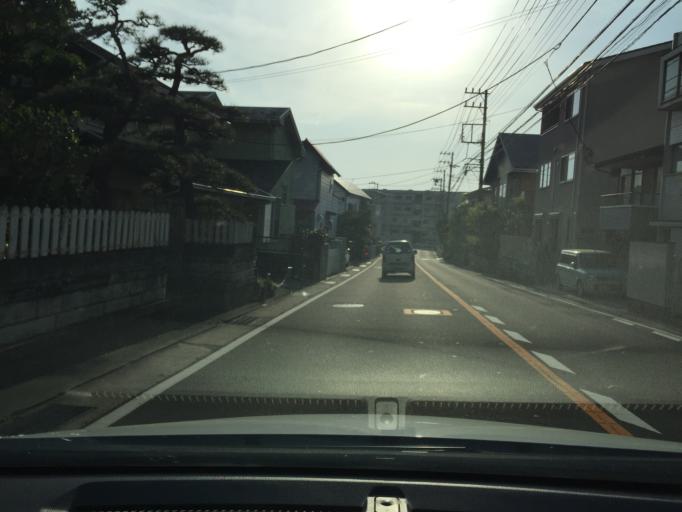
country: JP
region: Kanagawa
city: Zushi
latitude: 35.2852
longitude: 139.5720
